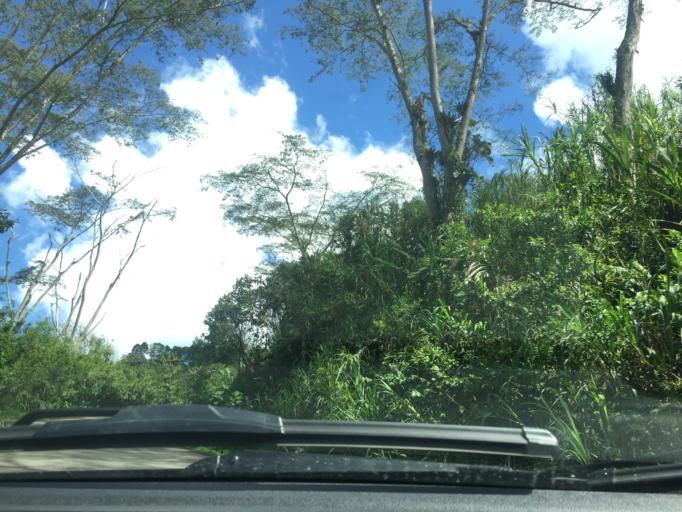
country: CO
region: Cundinamarca
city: San Francisco
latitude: 5.0133
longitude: -74.2741
